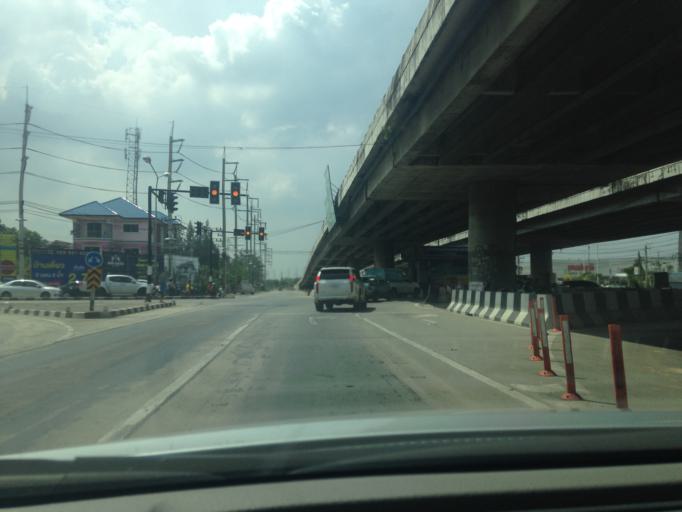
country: TH
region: Pathum Thani
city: Pathum Thani
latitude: 14.0298
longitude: 100.5261
